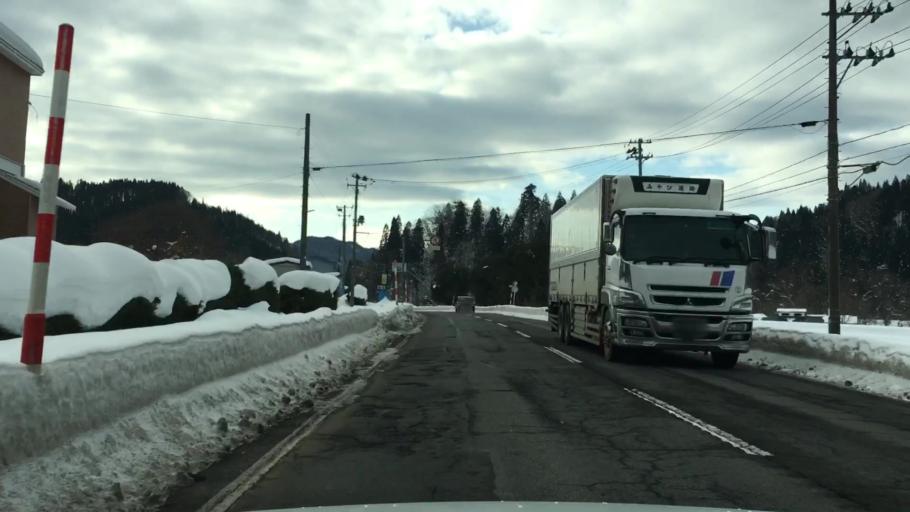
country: JP
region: Akita
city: Odate
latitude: 40.4523
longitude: 140.6353
